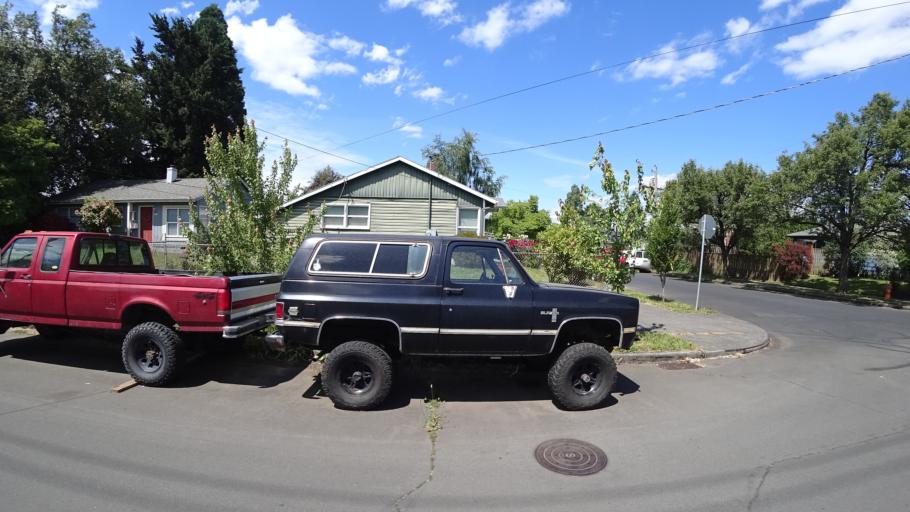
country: US
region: Oregon
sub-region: Washington County
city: West Haven
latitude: 45.5864
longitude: -122.7305
